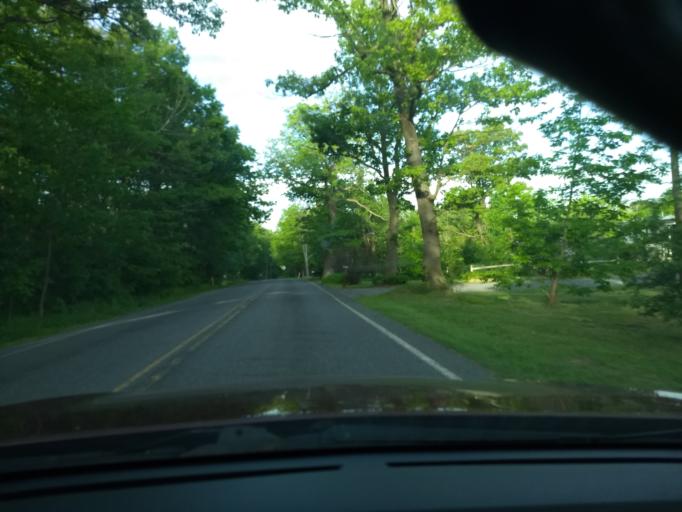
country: US
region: Pennsylvania
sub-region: Cambria County
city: Gallitzin
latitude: 40.5126
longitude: -78.5372
